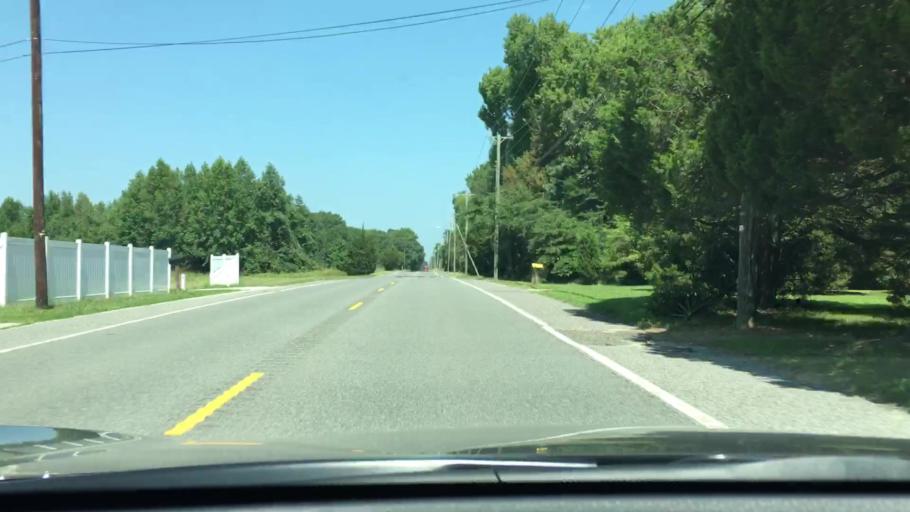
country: US
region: New Jersey
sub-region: Cumberland County
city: Laurel Lake
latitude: 39.3040
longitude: -75.0038
